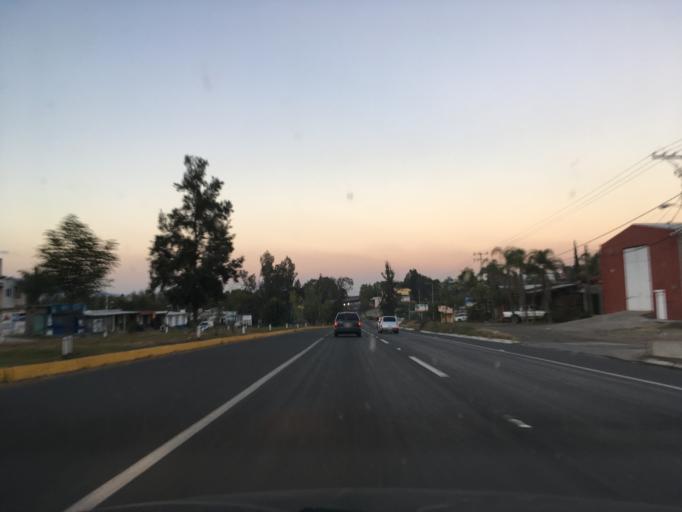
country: MX
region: Michoacan
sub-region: Morelia
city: Morelos
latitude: 19.6457
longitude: -101.2495
